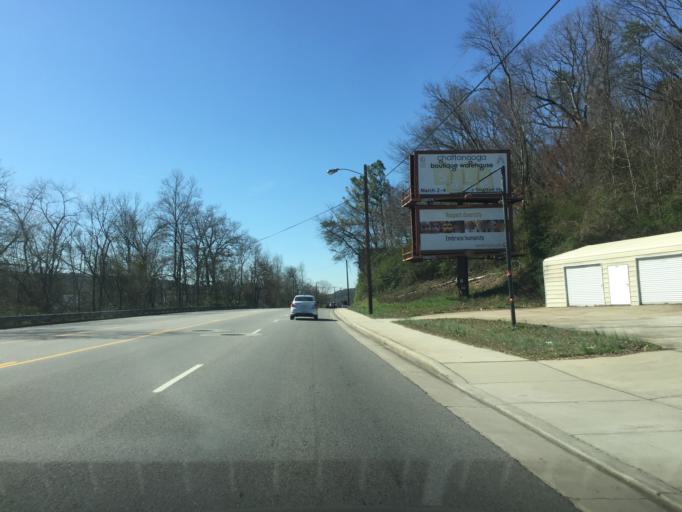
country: US
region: Tennessee
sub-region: Hamilton County
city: Red Bank
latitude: 35.0971
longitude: -85.3049
